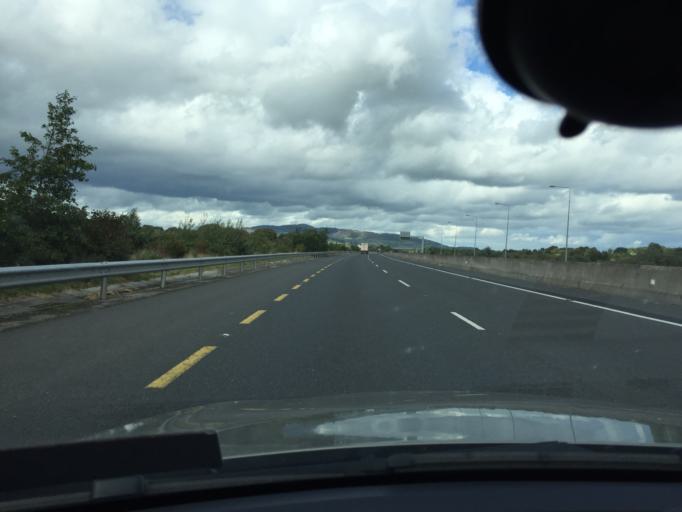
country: GB
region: Northern Ireland
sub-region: Newry and Mourne District
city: Newry
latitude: 54.1009
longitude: -6.3640
